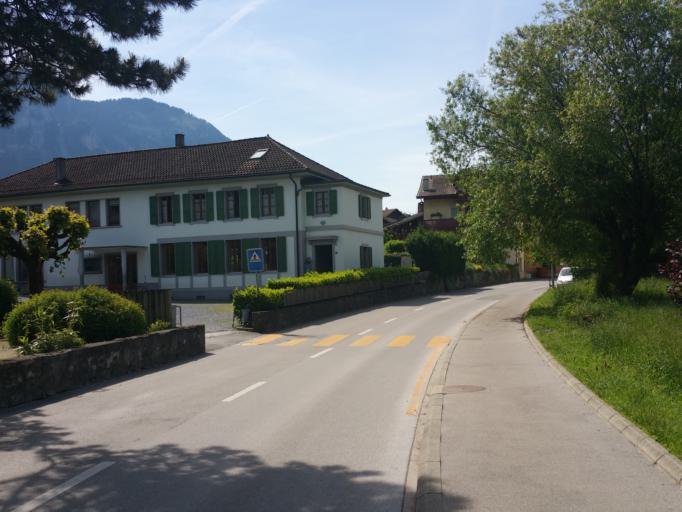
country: CH
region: Vaud
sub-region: Aigle District
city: Bex
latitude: 46.2476
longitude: 7.0126
